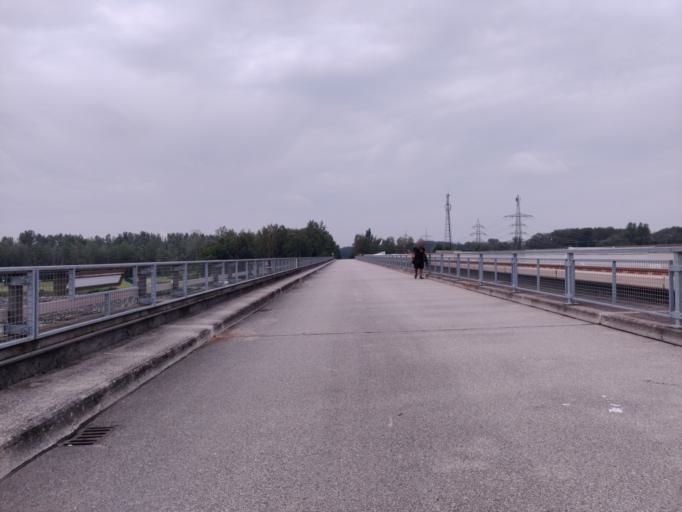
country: AT
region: Upper Austria
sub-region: Politischer Bezirk Linz-Land
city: Asten
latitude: 48.2483
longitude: 14.4310
